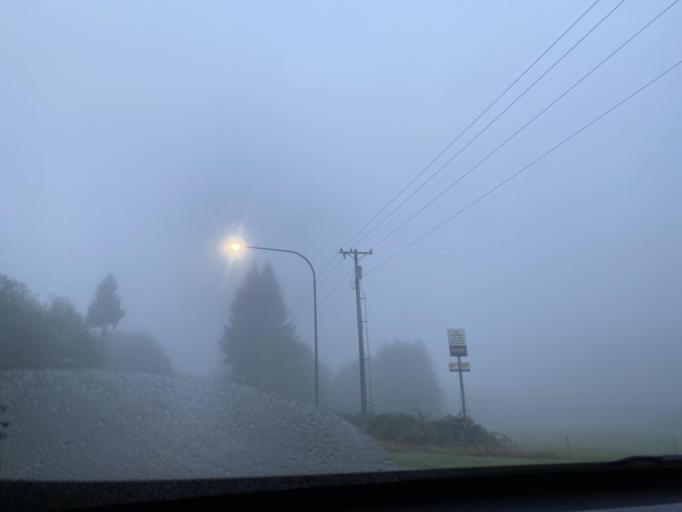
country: US
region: Washington
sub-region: Clallam County
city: Forks
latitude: 47.9347
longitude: -124.4016
